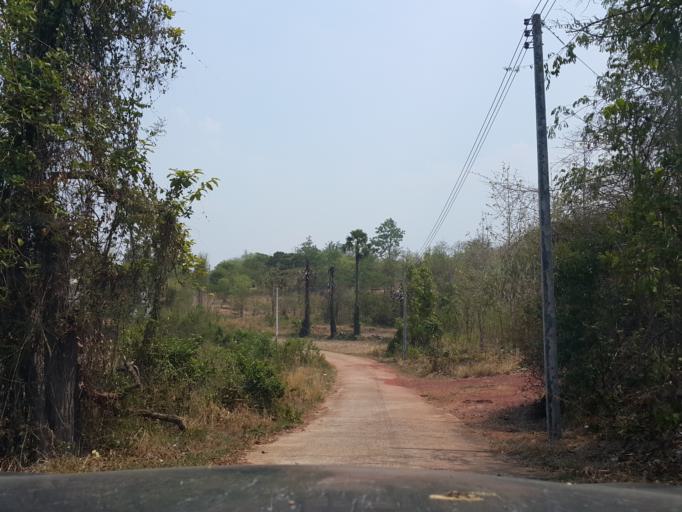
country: TH
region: Lampang
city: Mae Phrik
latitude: 17.5693
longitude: 99.0860
